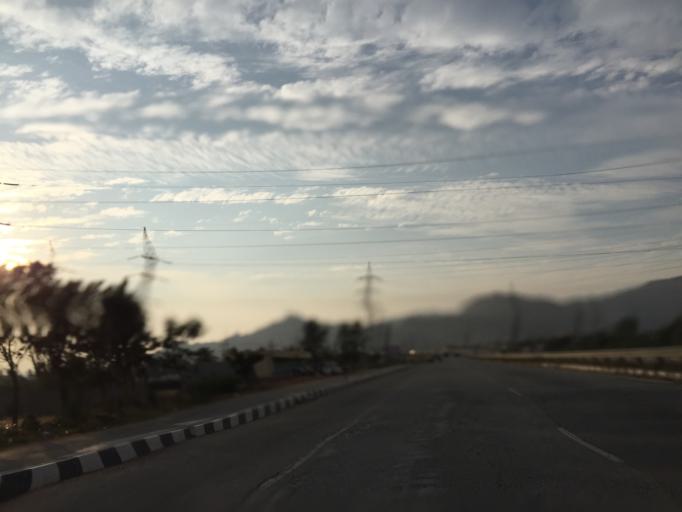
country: IN
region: Karnataka
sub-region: Kolar
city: Kolar
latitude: 13.1246
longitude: 78.1195
